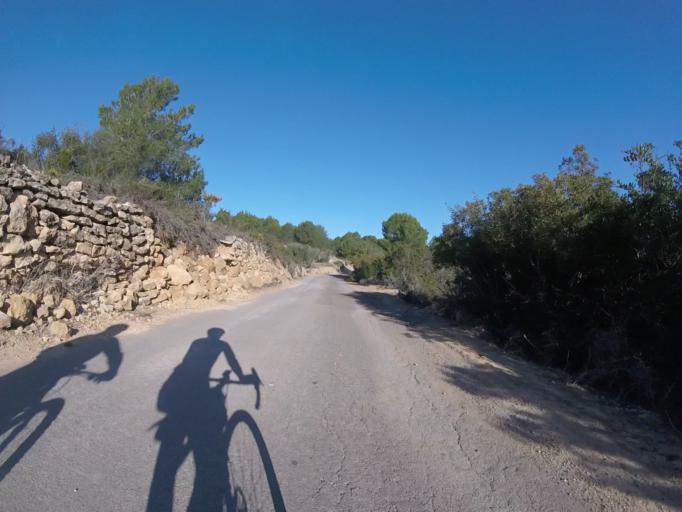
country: ES
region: Valencia
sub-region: Provincia de Castello
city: Alcala de Xivert
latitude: 40.2714
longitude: 0.2065
